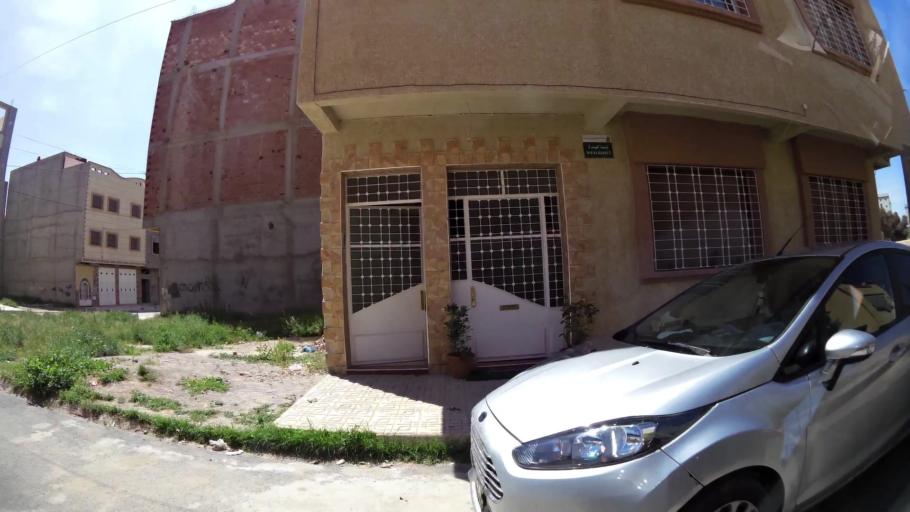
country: MA
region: Oriental
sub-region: Oujda-Angad
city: Oujda
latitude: 34.6493
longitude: -1.9098
